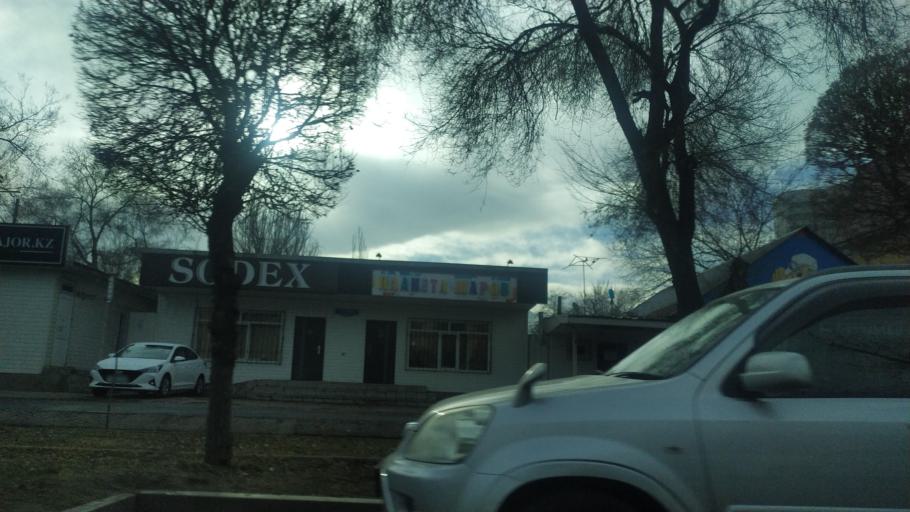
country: KZ
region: Almaty Qalasy
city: Almaty
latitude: 43.2375
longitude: 76.8860
